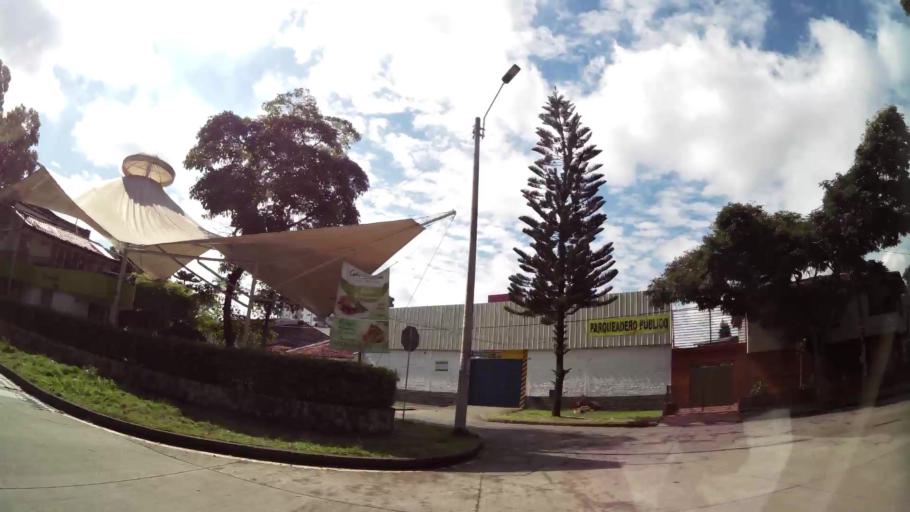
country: CO
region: Valle del Cauca
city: Cali
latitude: 3.4250
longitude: -76.5424
